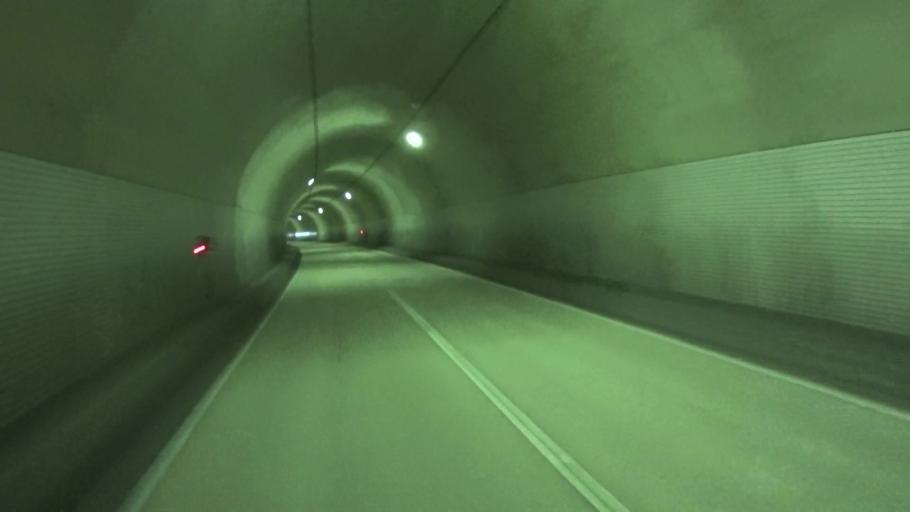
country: JP
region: Kyoto
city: Kameoka
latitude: 35.1064
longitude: 135.5585
